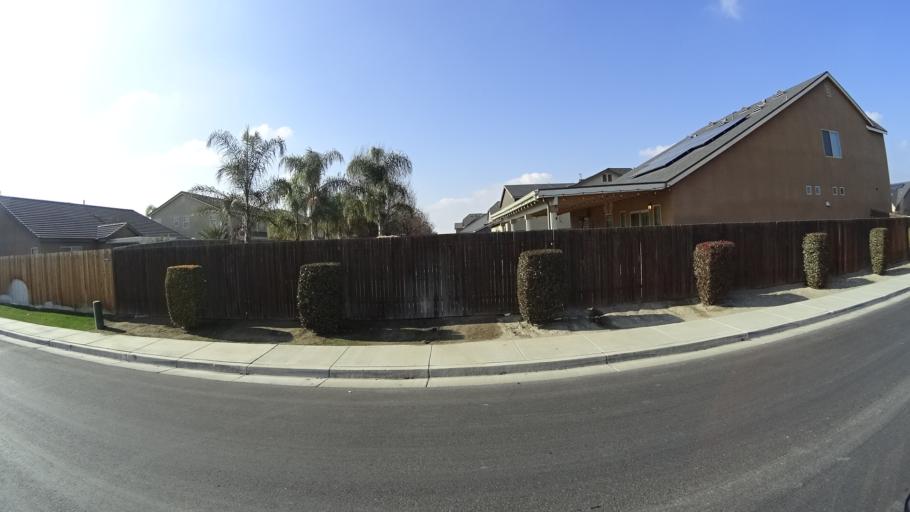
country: US
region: California
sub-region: Kern County
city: Greenacres
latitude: 35.3025
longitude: -119.1038
